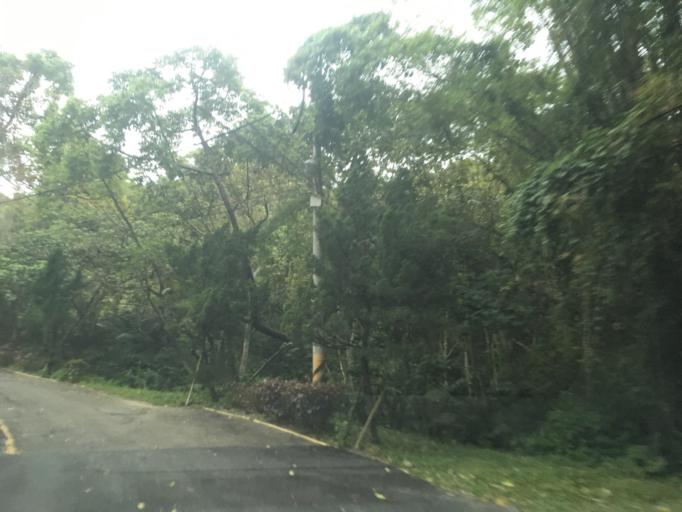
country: TW
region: Taiwan
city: Zhongxing New Village
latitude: 24.0343
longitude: 120.7466
